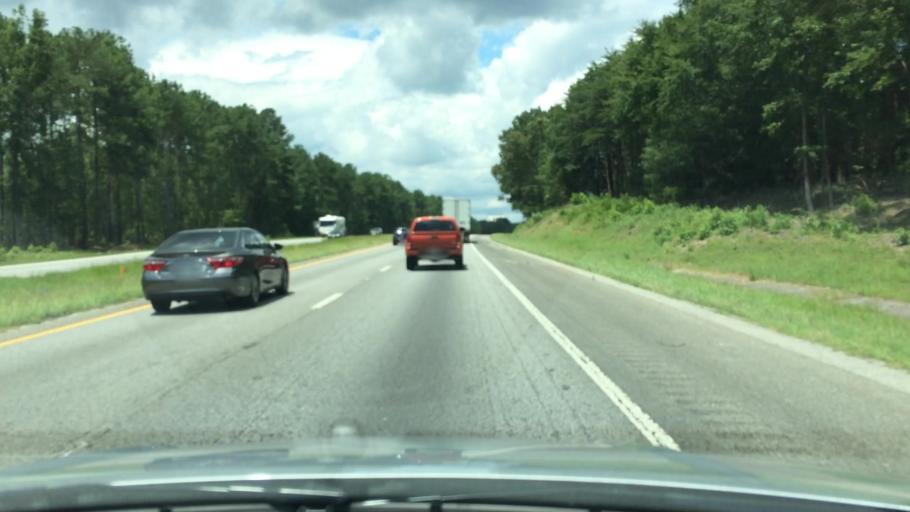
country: US
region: South Carolina
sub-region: Spartanburg County
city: Woodruff
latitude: 34.7347
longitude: -81.9526
